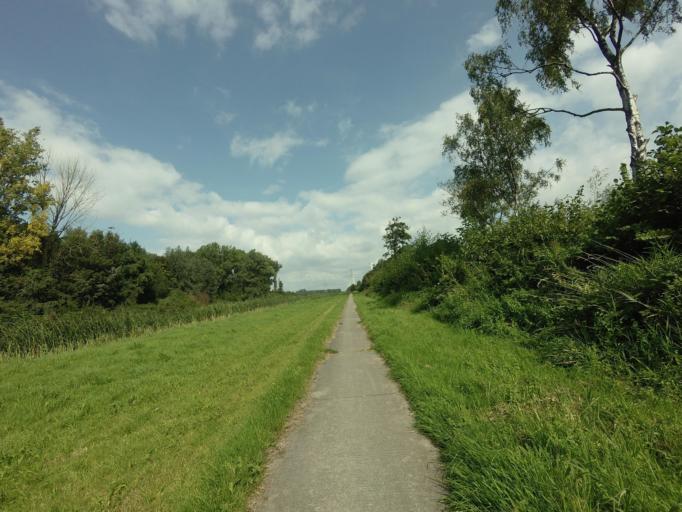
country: NL
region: Flevoland
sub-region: Gemeente Lelystad
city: Lelystad
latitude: 52.5527
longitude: 5.5367
